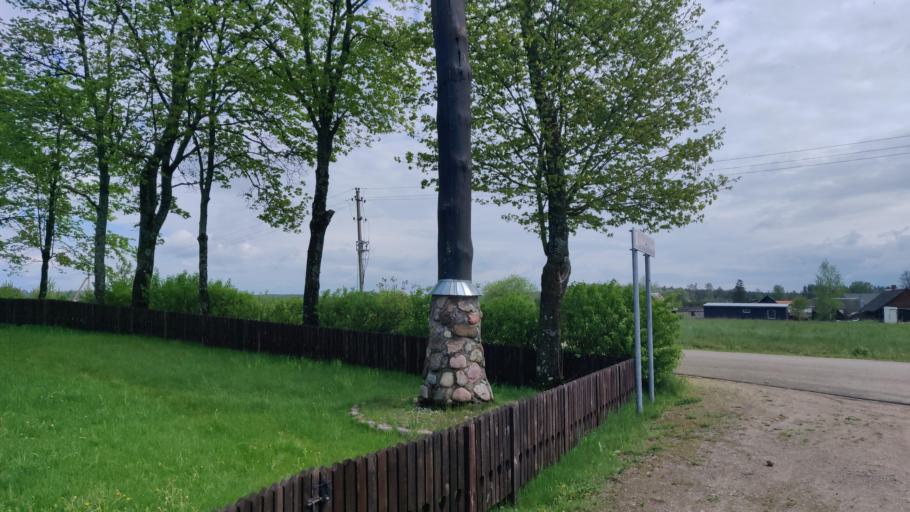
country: LT
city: Baltoji Voke
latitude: 54.5517
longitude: 25.1223
